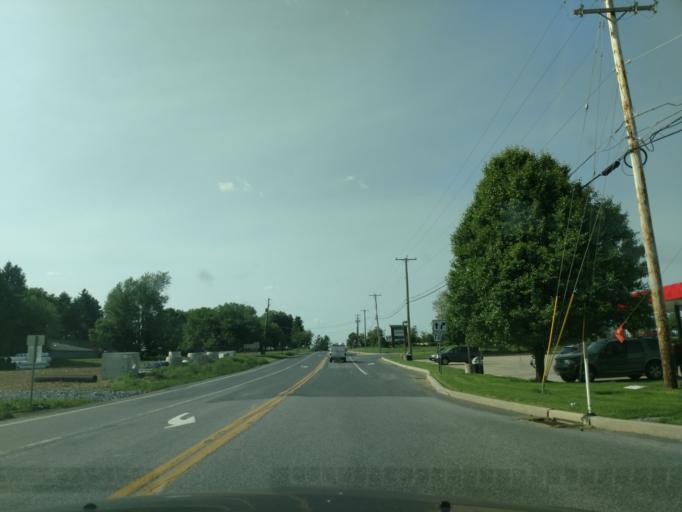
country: US
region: Pennsylvania
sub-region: Lebanon County
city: Lebanon South
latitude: 40.3048
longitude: -76.4238
